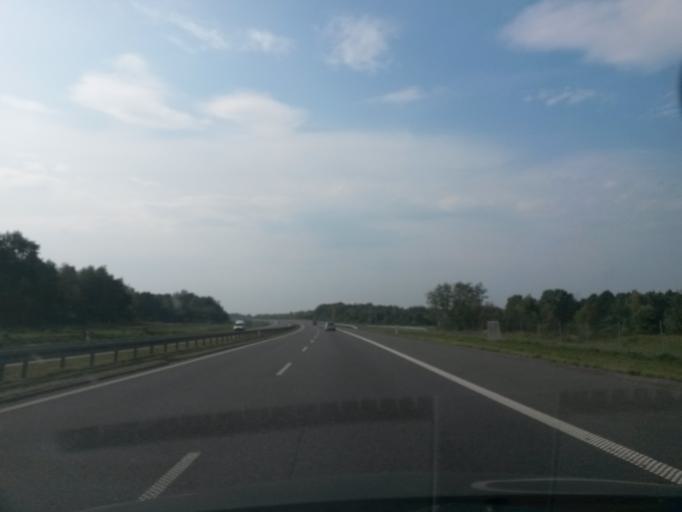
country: PL
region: Lesser Poland Voivodeship
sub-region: Powiat bochenski
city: Borek
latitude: 50.0066
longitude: 20.5375
